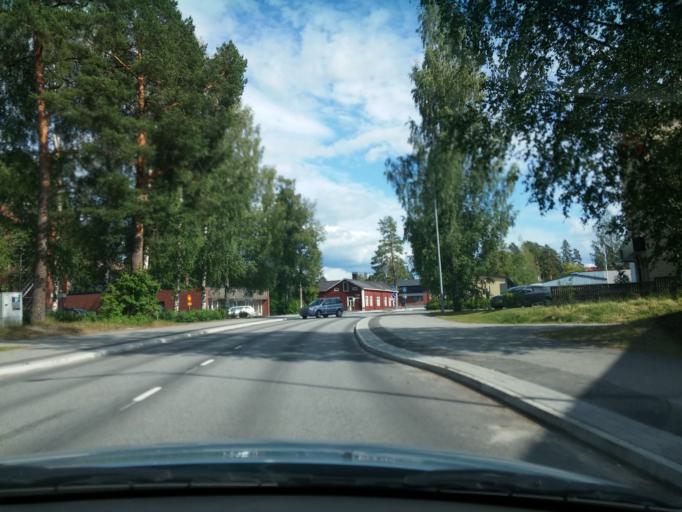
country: FI
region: Central Finland
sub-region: Keuruu
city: Keuruu
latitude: 62.2633
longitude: 24.7017
